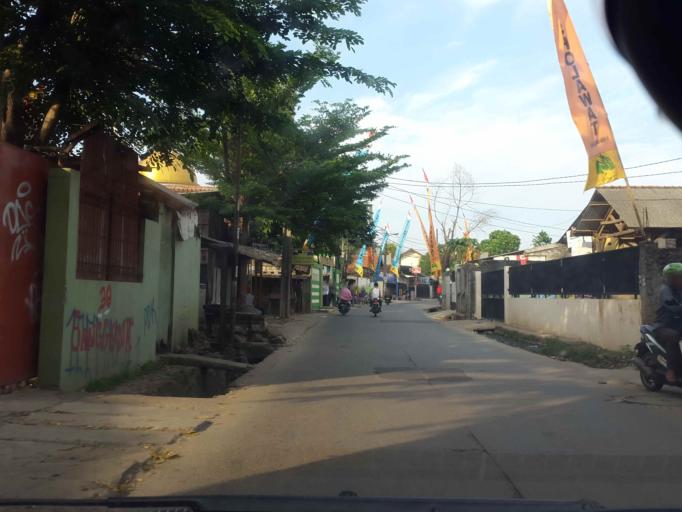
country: ID
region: West Java
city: Ciputat
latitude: -6.2464
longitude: 106.6890
